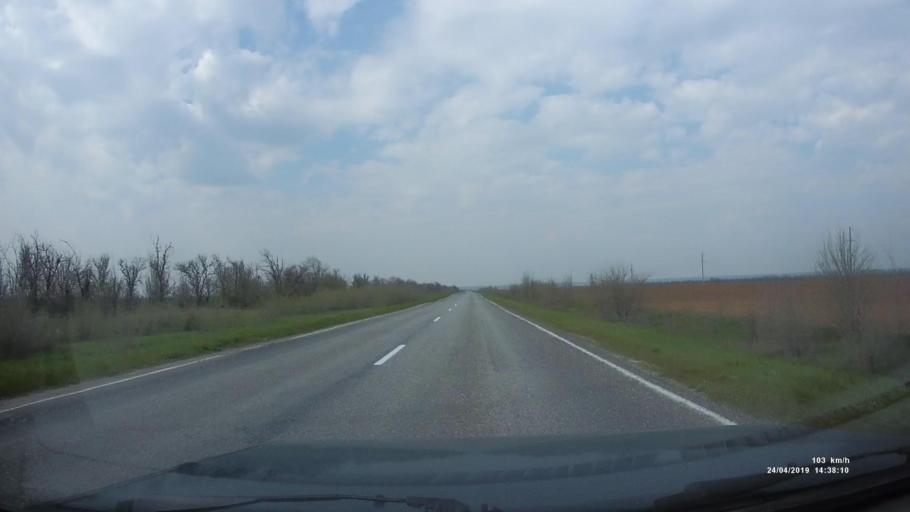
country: RU
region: Rostov
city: Remontnoye
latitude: 46.3967
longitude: 43.8861
